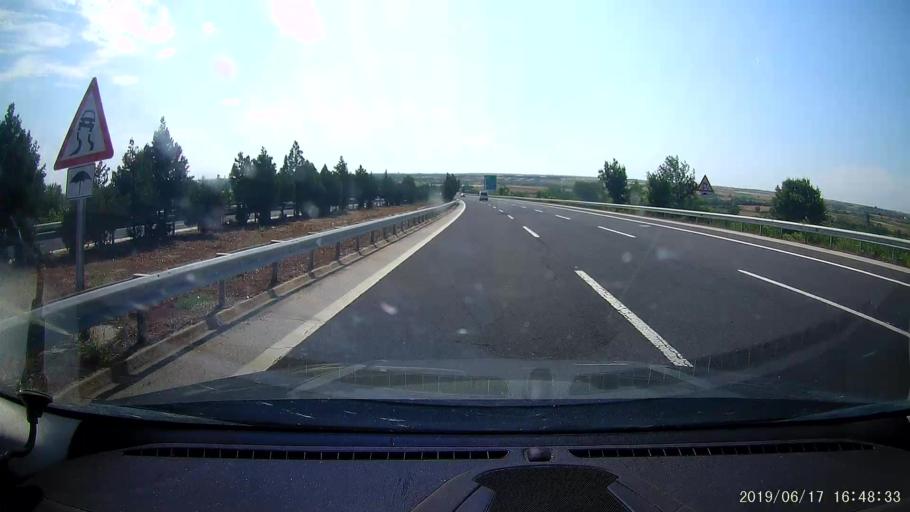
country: TR
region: Kirklareli
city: Babaeski
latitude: 41.5067
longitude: 27.1384
